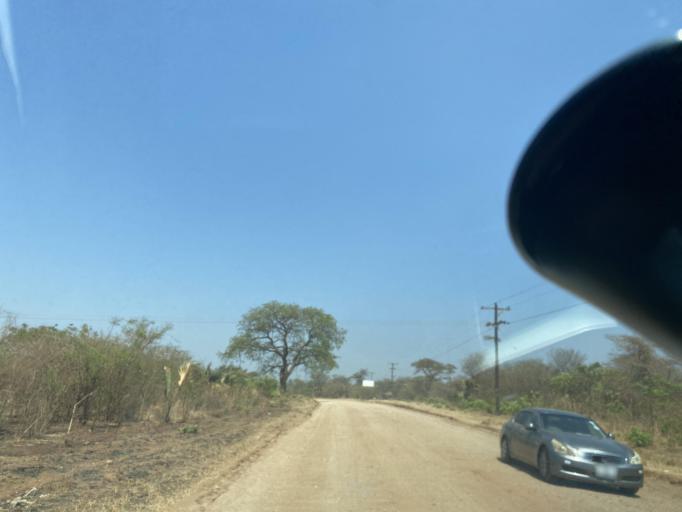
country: ZM
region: Lusaka
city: Lusaka
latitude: -15.5248
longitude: 28.1050
